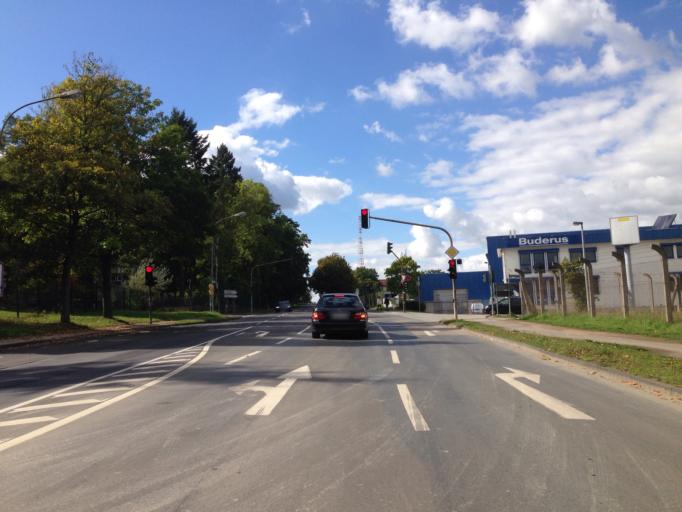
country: DE
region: Hesse
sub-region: Regierungsbezirk Giessen
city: Giessen
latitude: 50.5901
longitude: 8.7181
